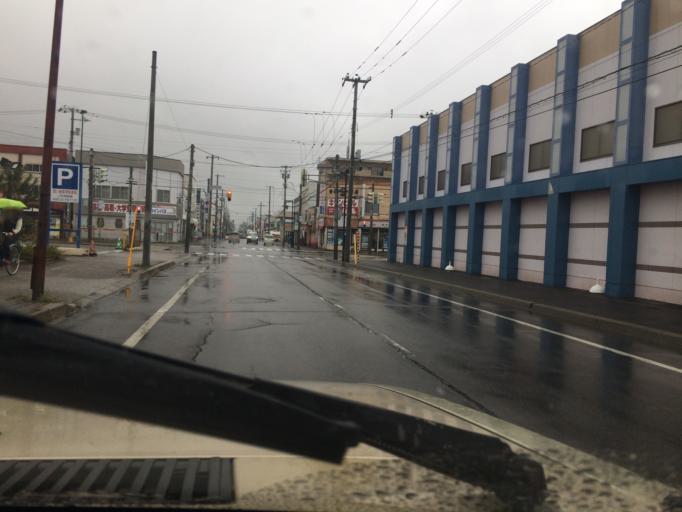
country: JP
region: Hokkaido
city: Obihiro
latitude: 42.9104
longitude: 143.0499
